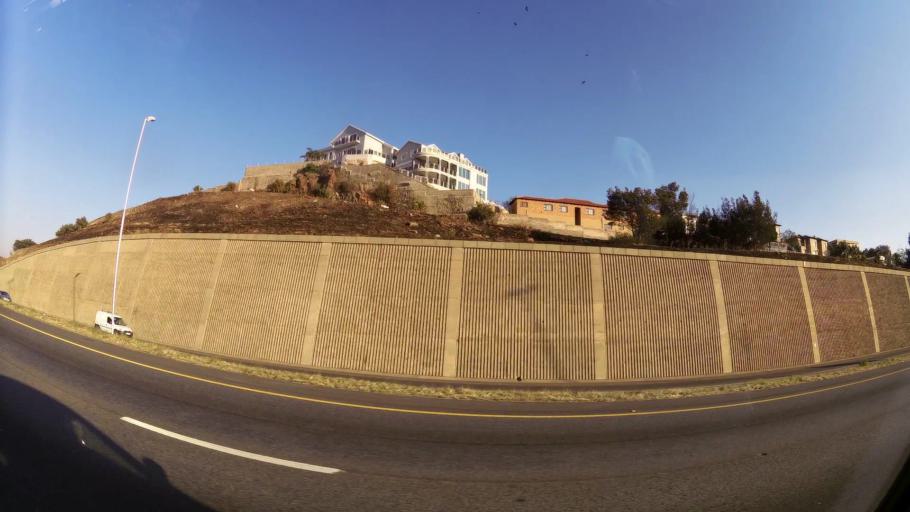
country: ZA
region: Gauteng
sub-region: City of Johannesburg Metropolitan Municipality
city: Johannesburg
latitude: -26.2690
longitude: 28.0641
